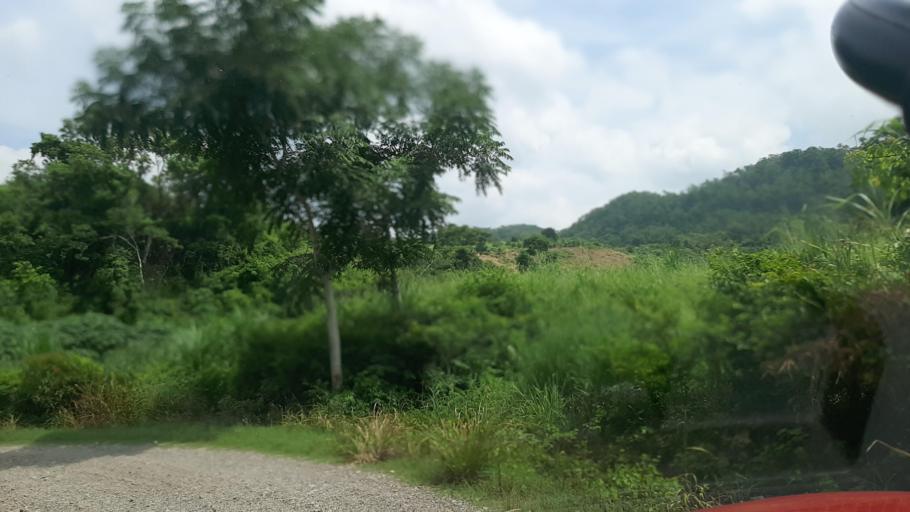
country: MX
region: Veracruz
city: Gutierrez Zamora
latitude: 20.4480
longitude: -97.1756
